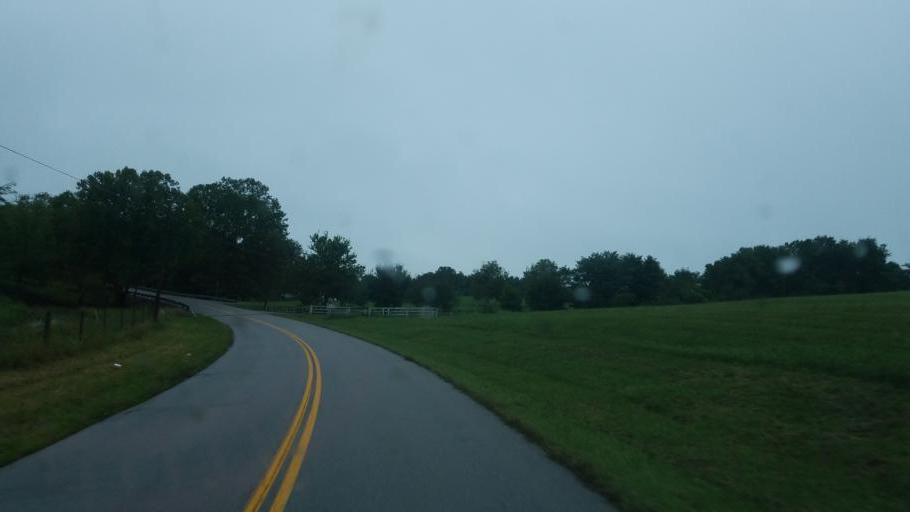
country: US
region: Kentucky
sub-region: Fleming County
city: Flemingsburg
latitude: 38.4259
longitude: -83.7106
